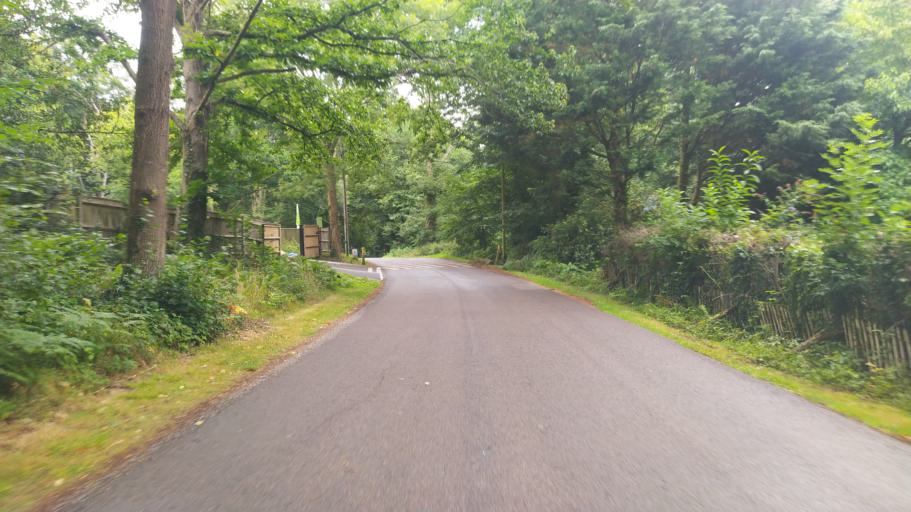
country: GB
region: England
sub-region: Hampshire
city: Hedge End
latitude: 50.8986
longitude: -1.3021
